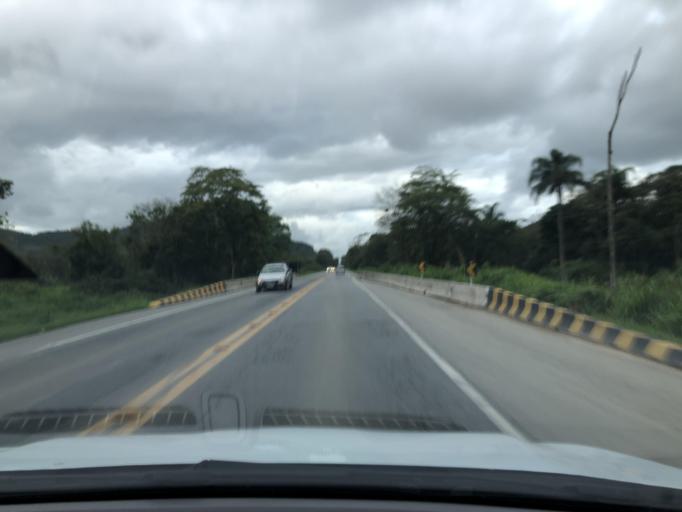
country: BR
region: Santa Catarina
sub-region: Sao Francisco Do Sul
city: Sao Francisco do Sul
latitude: -26.3278
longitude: -48.6505
